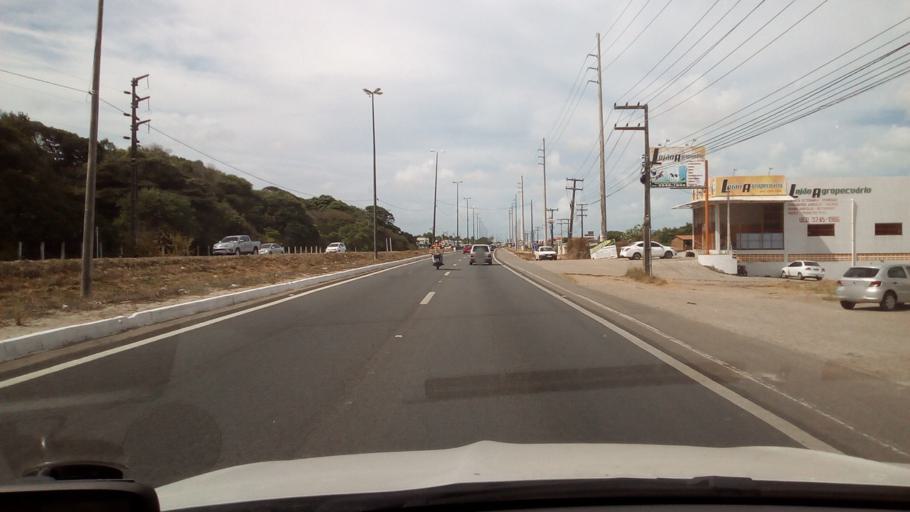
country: BR
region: Paraiba
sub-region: Joao Pessoa
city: Joao Pessoa
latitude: -7.0636
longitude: -34.8502
